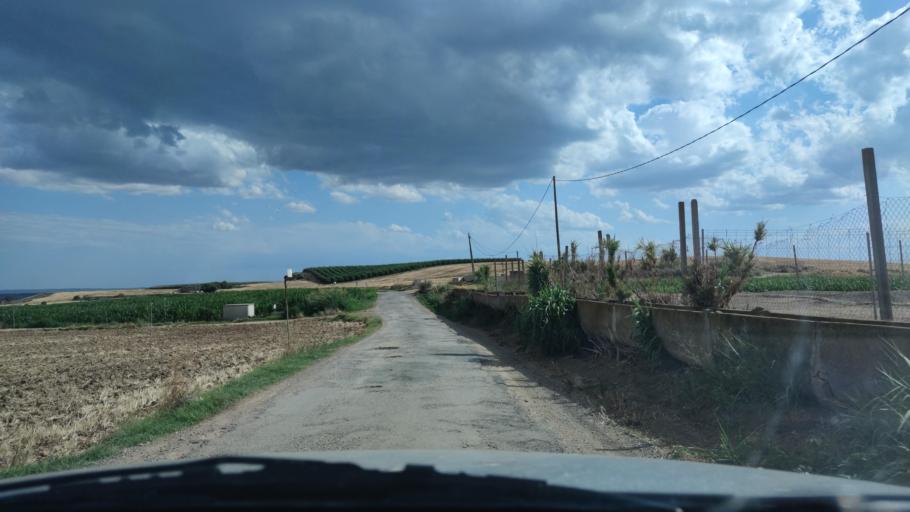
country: ES
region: Catalonia
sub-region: Provincia de Lleida
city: Alcarras
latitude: 41.5978
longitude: 0.5419
